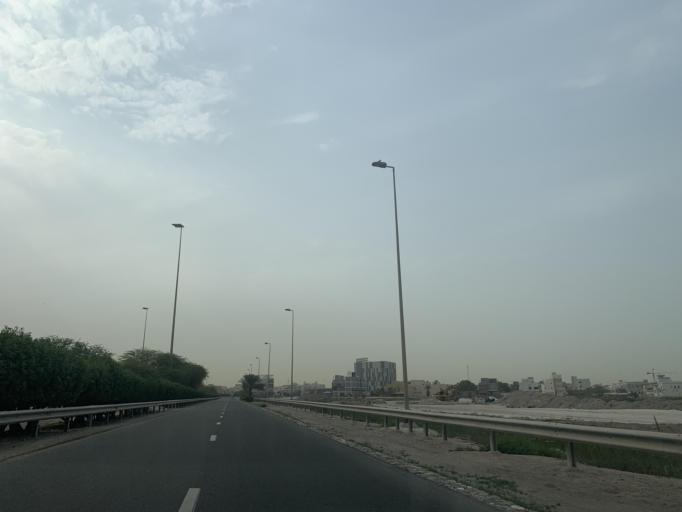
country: BH
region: Manama
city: Jidd Hafs
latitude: 26.1966
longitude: 50.5378
